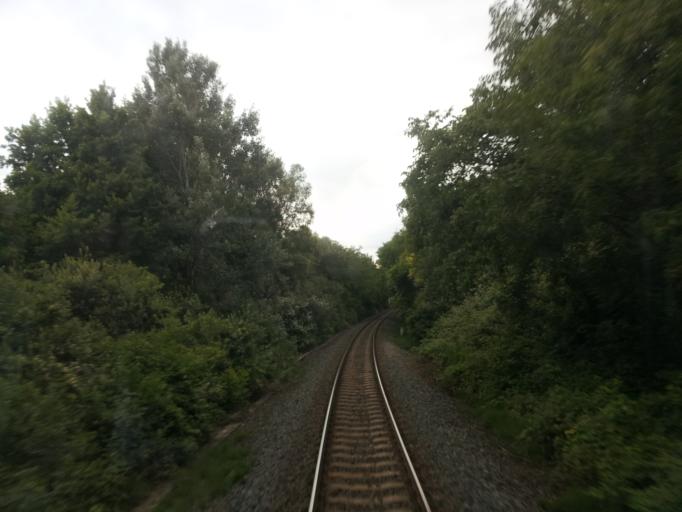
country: HU
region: Veszprem
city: Balatonalmadi
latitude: 47.0449
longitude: 18.0268
